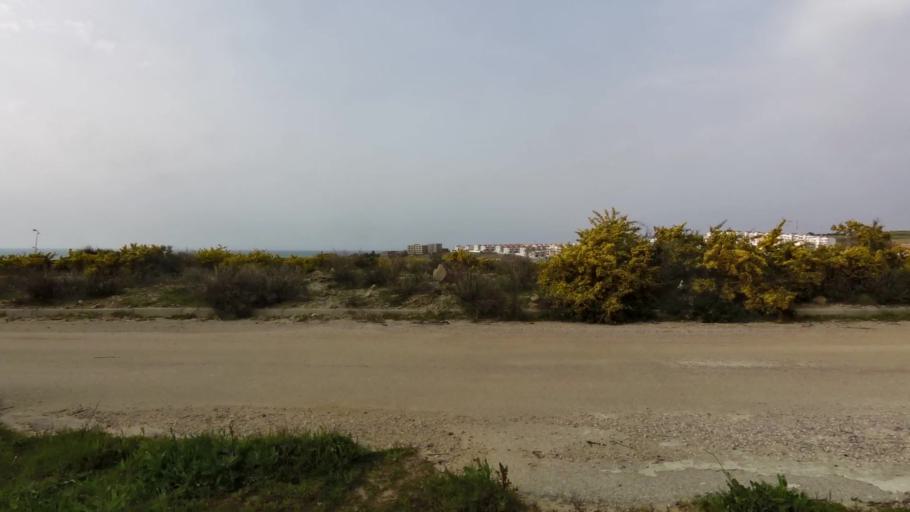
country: MA
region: Tanger-Tetouan
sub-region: Tanger-Assilah
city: Boukhalef
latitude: 35.7000
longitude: -5.9404
